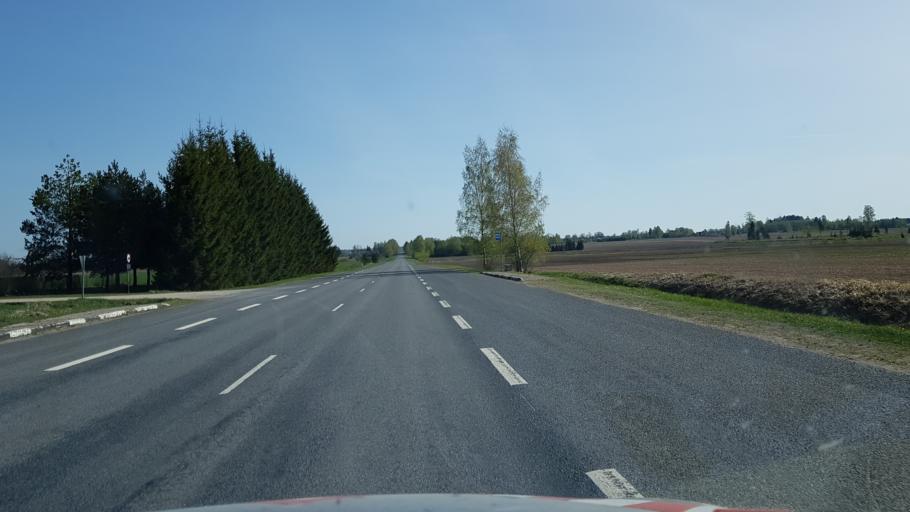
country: EE
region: Viljandimaa
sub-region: Karksi vald
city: Karksi-Nuia
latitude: 58.1780
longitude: 25.4930
